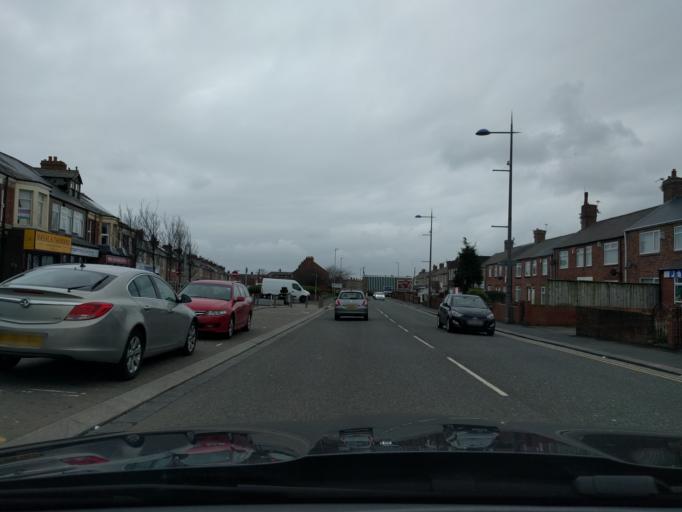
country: GB
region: England
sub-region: Northumberland
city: Ashington
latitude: 55.1819
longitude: -1.5685
